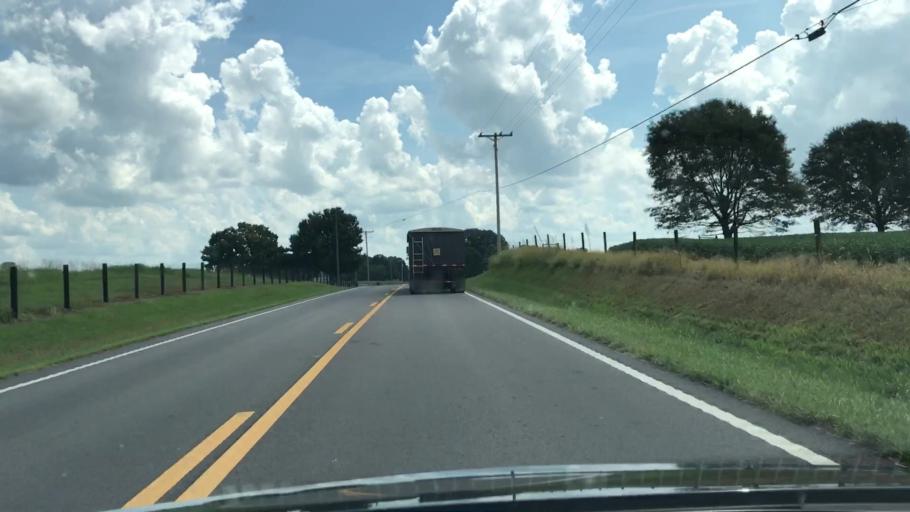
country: US
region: Tennessee
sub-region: Robertson County
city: Springfield
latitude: 36.6094
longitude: -86.9306
